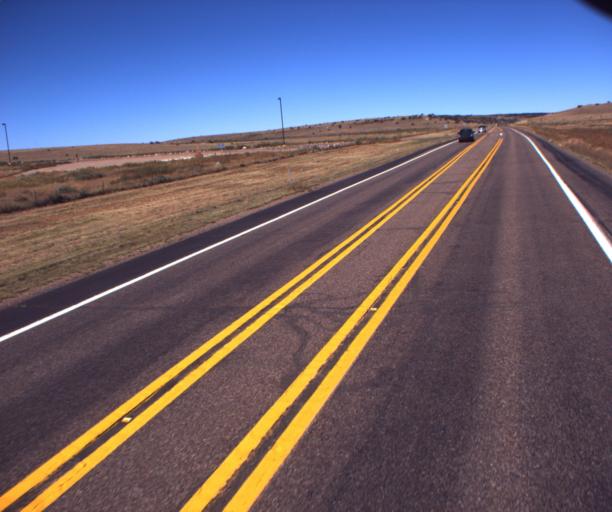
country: US
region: Arizona
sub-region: Apache County
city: Saint Johns
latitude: 34.3214
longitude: -109.3835
